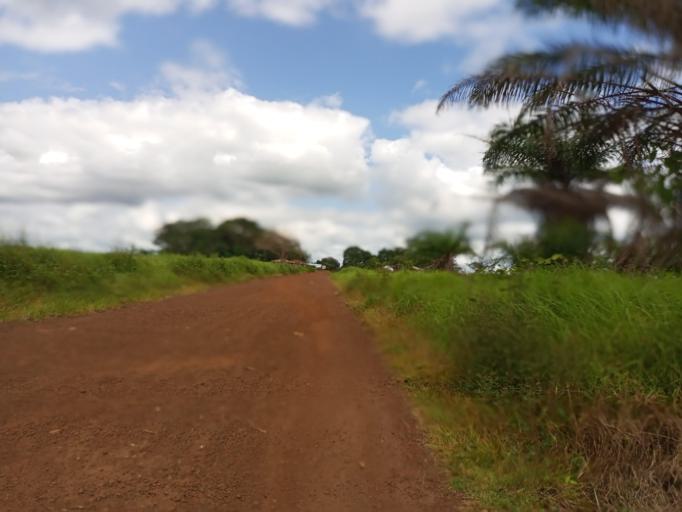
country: SL
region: Northern Province
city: Kamakwie
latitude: 9.5069
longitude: -12.2278
